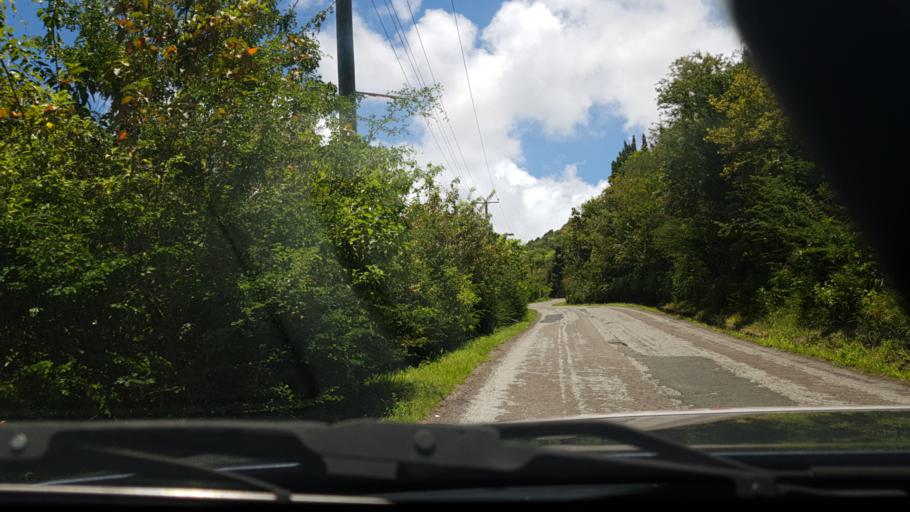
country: LC
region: Anse-la-Raye
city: Anse La Raye
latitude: 13.9278
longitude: -61.0449
